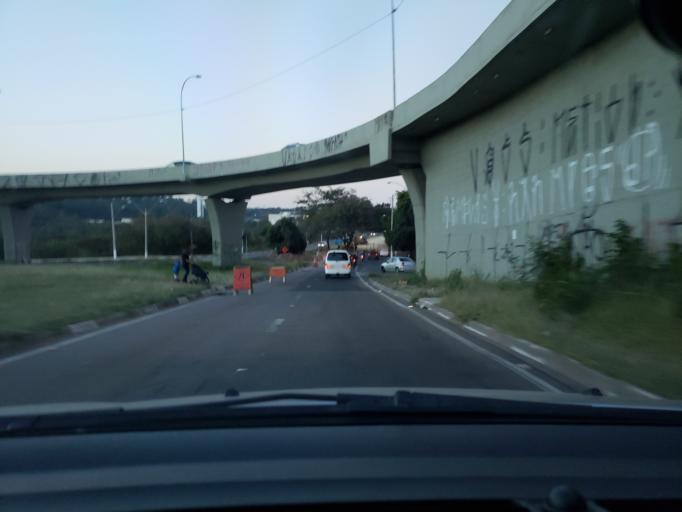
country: BR
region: Sao Paulo
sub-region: Campinas
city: Campinas
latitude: -22.9248
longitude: -47.1244
